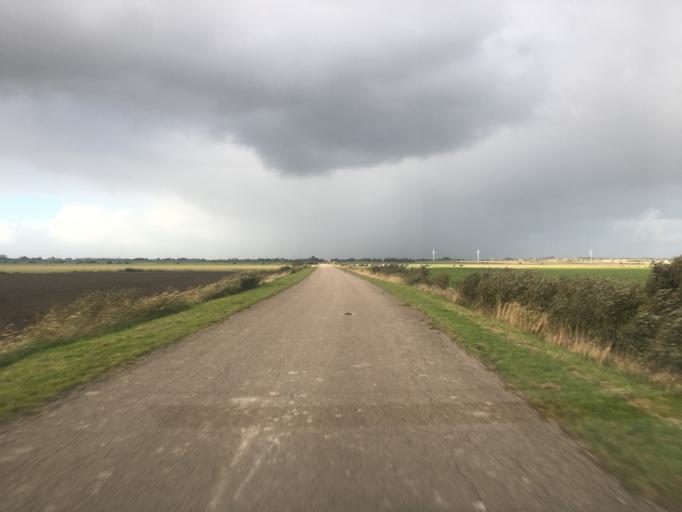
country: DE
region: Schleswig-Holstein
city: Aventoft
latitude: 54.9272
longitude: 8.7732
